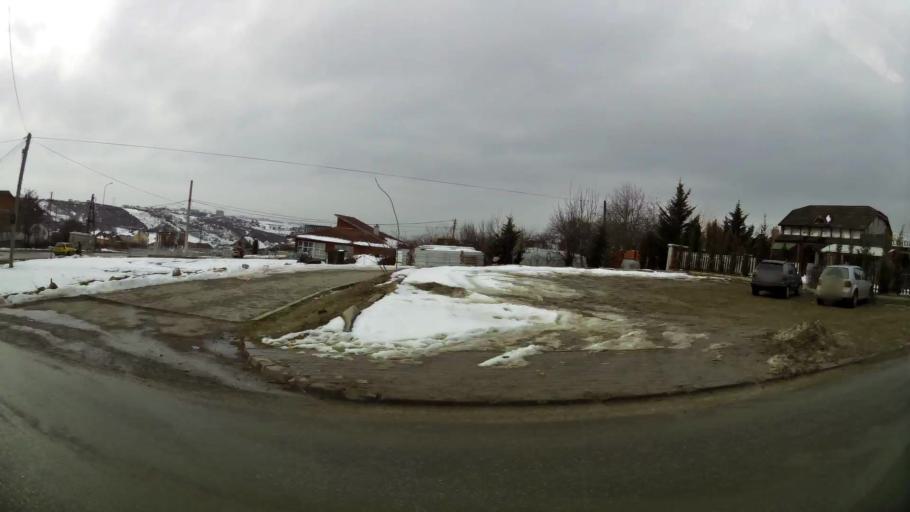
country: XK
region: Pristina
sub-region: Komuna e Prishtines
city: Pristina
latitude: 42.6458
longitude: 21.1954
